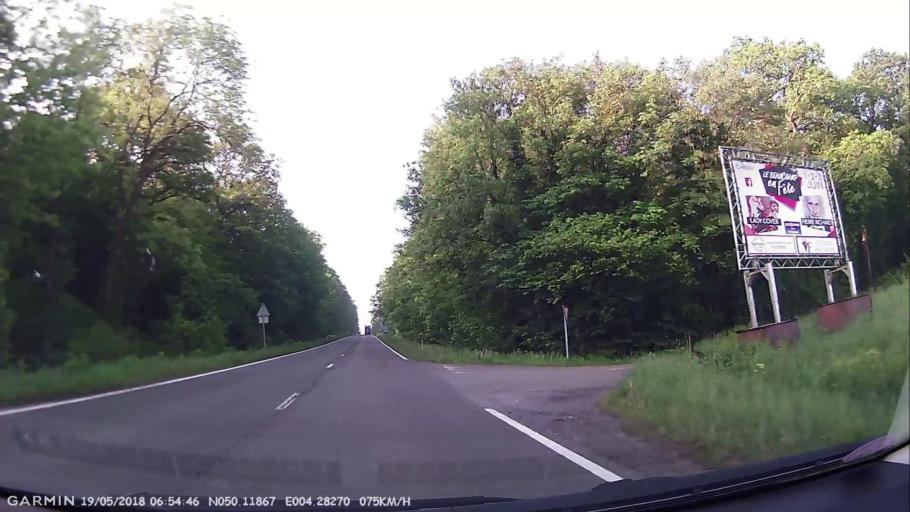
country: BE
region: Wallonia
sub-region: Province du Hainaut
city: Froidchapelle
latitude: 50.1184
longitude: 4.2828
